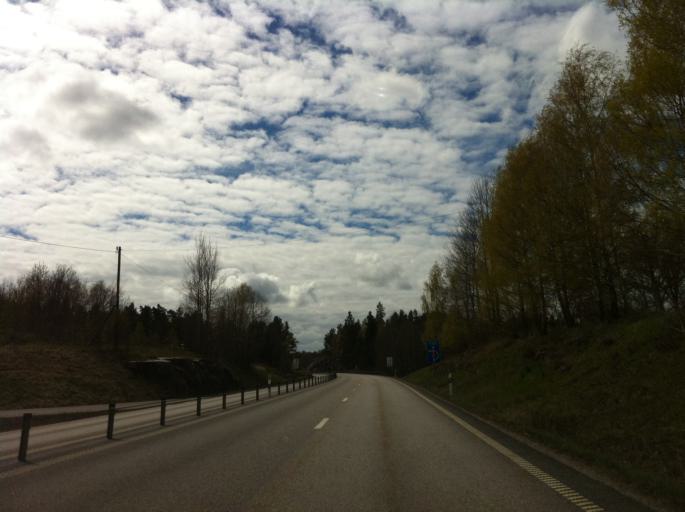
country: SE
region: OEstergoetland
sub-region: Valdemarsviks Kommun
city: Valdemarsvik
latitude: 58.1678
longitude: 16.5554
